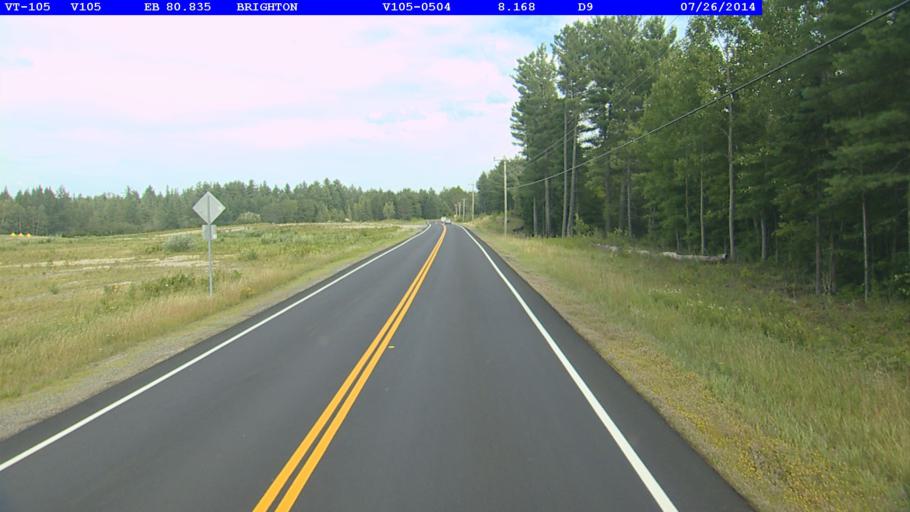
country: US
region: New Hampshire
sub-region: Coos County
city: Stratford
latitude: 44.7871
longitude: -71.8237
